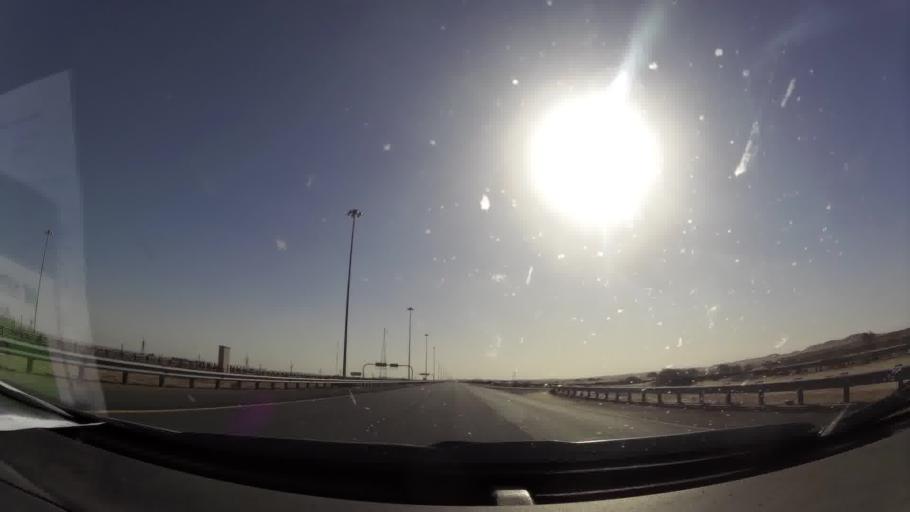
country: KW
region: Al Asimah
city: Kuwait City
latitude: 29.6061
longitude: 47.9134
